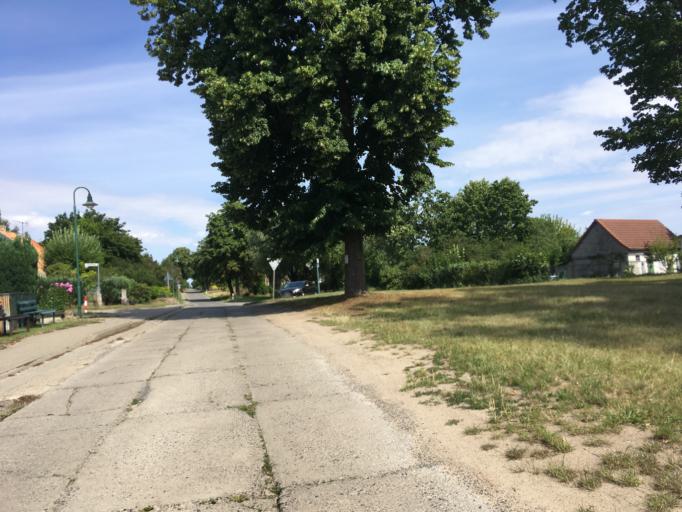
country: DE
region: Brandenburg
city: Casekow
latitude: 53.2077
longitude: 14.1512
